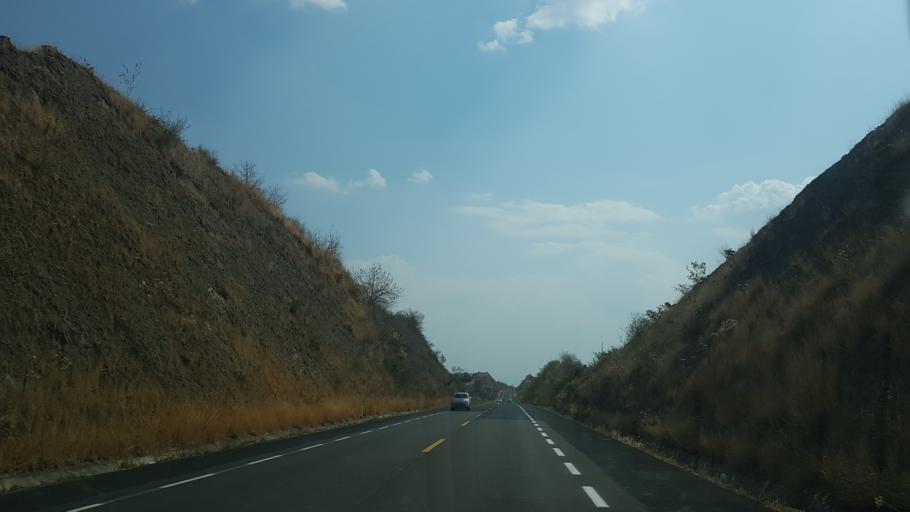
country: MX
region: Morelos
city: Tlacotepec
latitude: 18.8068
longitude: -98.7052
